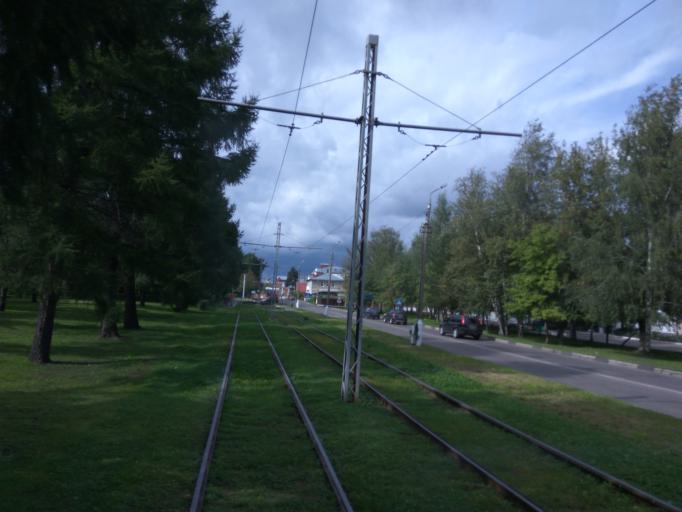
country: RU
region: Moskovskaya
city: Kolomna
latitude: 55.0950
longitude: 38.7724
